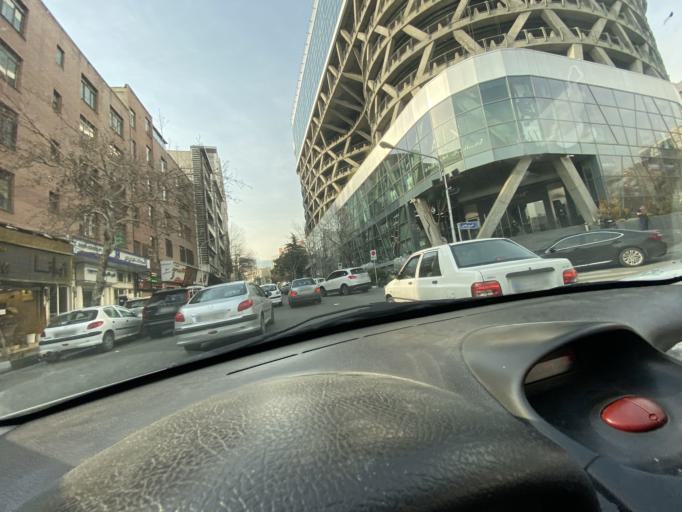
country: IR
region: Tehran
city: Tajrish
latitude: 35.8045
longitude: 51.4770
